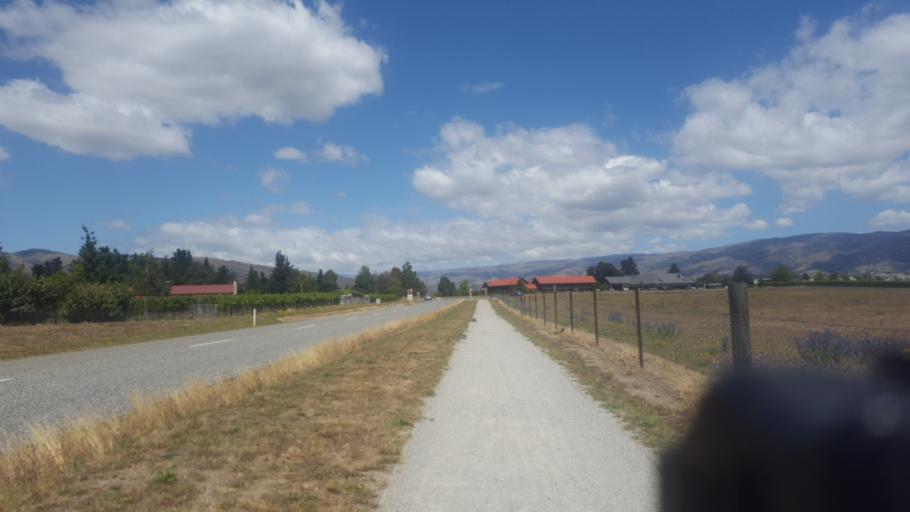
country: NZ
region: Otago
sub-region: Queenstown-Lakes District
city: Wanaka
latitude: -45.0327
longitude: 169.2028
